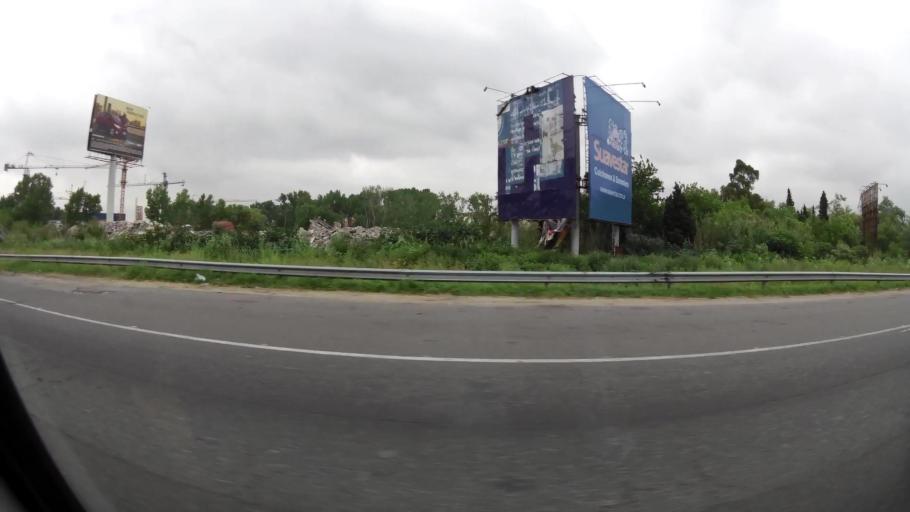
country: AR
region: Buenos Aires
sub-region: Partido de Avellaneda
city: Avellaneda
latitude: -34.6795
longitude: -58.3214
